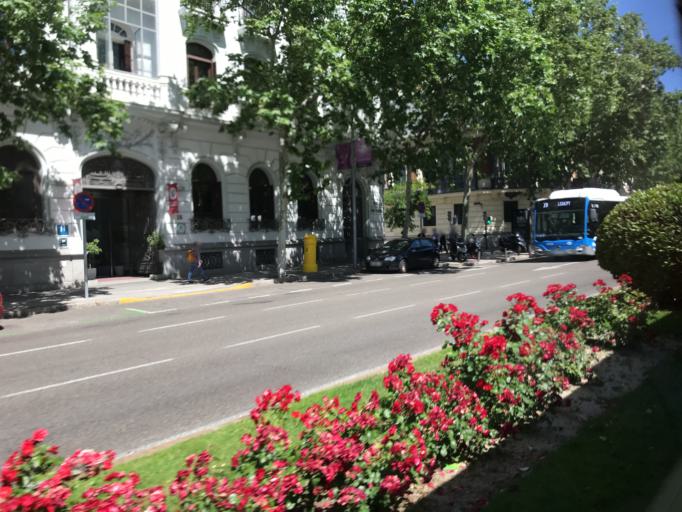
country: ES
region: Madrid
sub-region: Provincia de Madrid
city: Retiro
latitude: 40.4169
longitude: -3.6890
